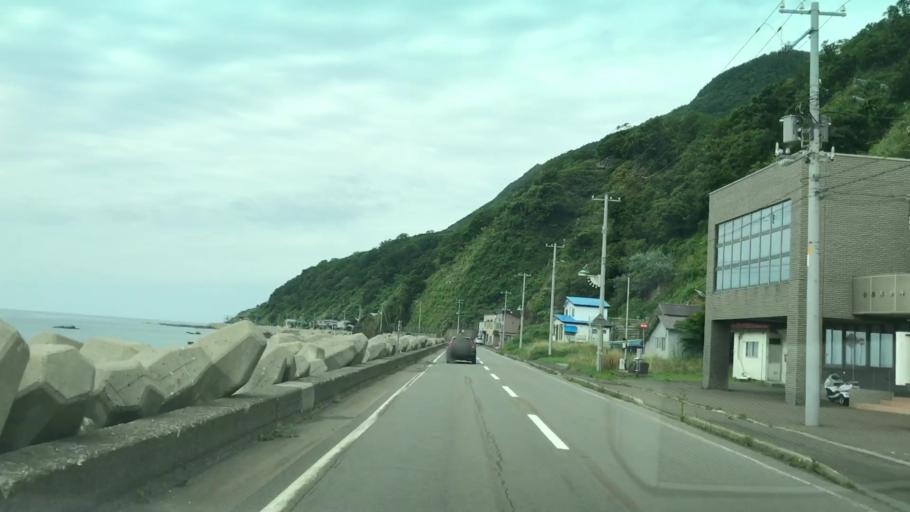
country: JP
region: Hokkaido
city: Iwanai
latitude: 43.1582
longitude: 140.4019
